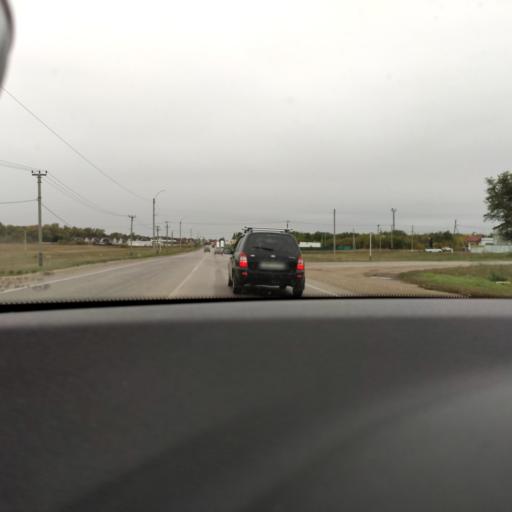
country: RU
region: Samara
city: Krasnyy Yar
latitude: 53.4830
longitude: 50.3912
